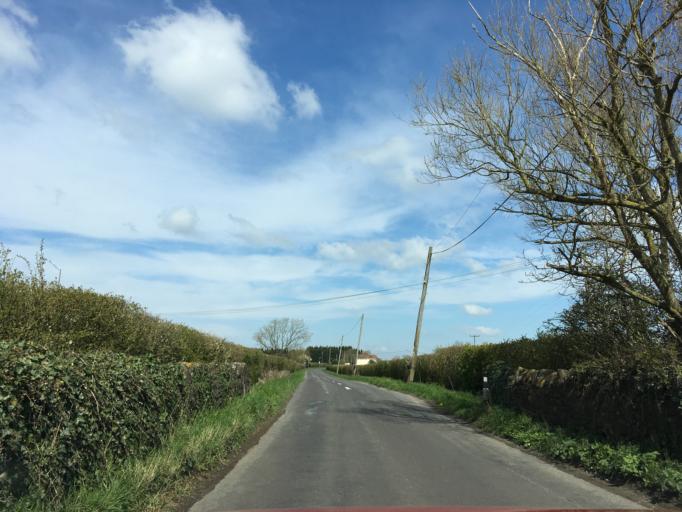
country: GB
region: England
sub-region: South Gloucestershire
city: Severn Beach
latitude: 51.5510
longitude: -2.6262
